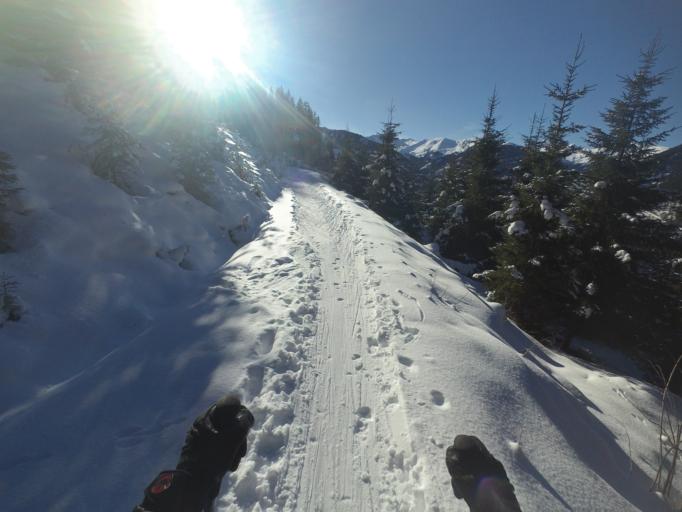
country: AT
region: Salzburg
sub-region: Politischer Bezirk Sankt Johann im Pongau
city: Huttschlag
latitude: 47.1804
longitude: 13.2749
